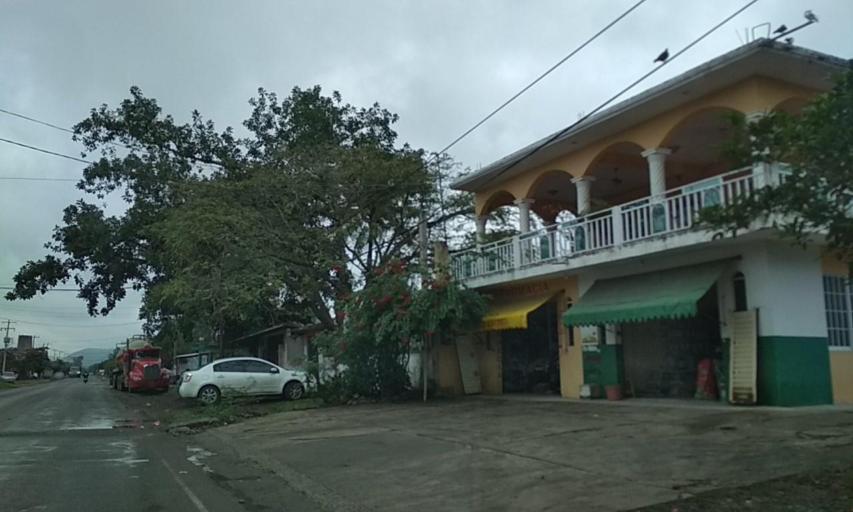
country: MX
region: Veracruz
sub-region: Papantla
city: El Chote
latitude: 20.3719
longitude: -97.3337
